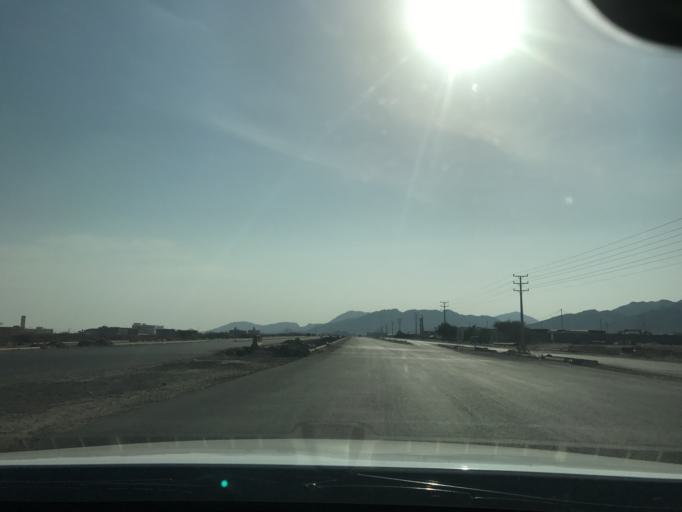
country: SA
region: Makkah
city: Al Jumum
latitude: 21.4545
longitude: 39.5474
